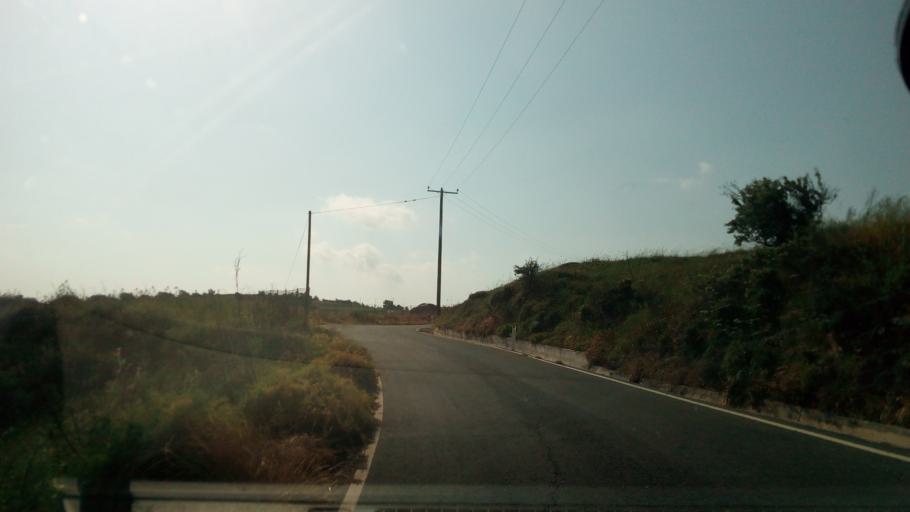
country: CY
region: Pafos
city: Pegeia
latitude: 34.9669
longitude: 32.3769
